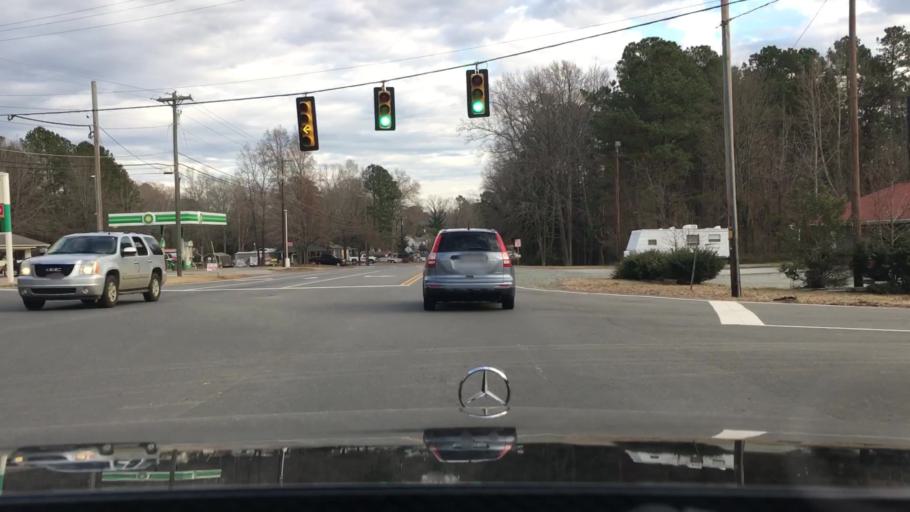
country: US
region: North Carolina
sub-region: Orange County
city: Hillsborough
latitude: 36.0820
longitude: -79.0797
